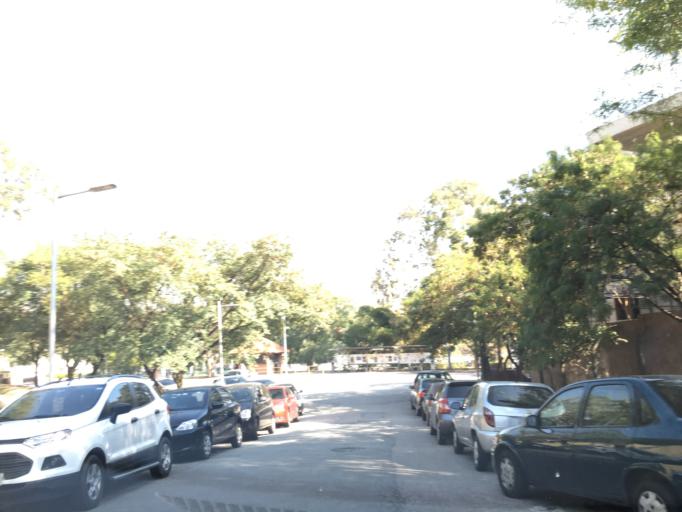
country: BR
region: Sao Paulo
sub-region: Osasco
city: Osasco
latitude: -23.5674
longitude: -46.7402
